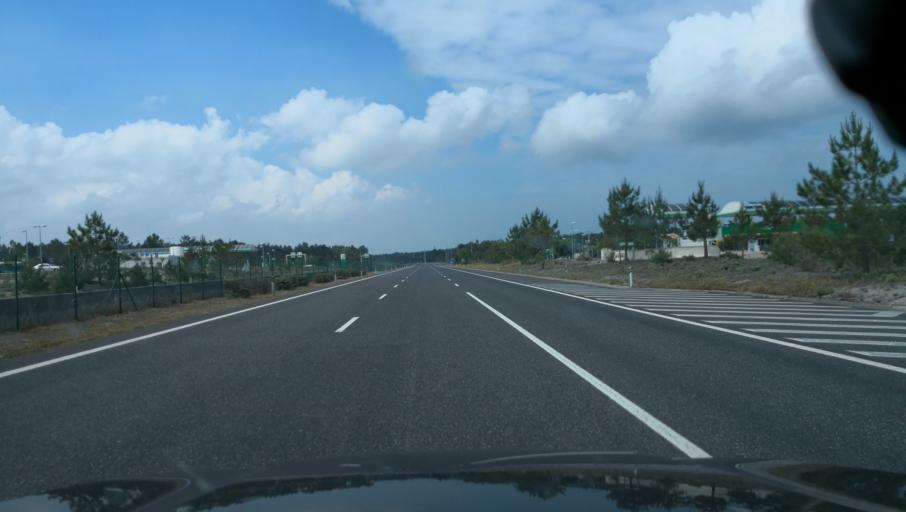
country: PT
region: Leiria
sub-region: Alcobaca
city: Pataias
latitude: 39.6214
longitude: -8.9898
